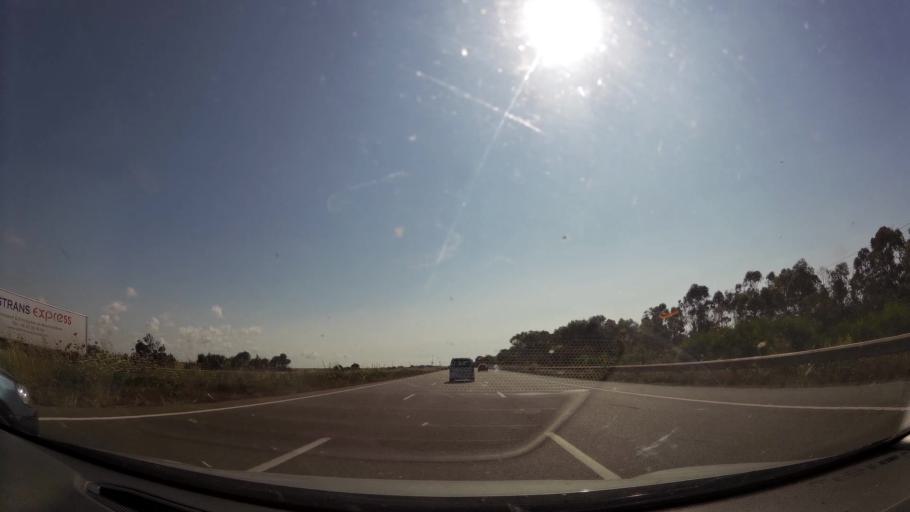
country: MA
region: Chaouia-Ouardigha
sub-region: Benslimane
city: Bouznika
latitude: 33.7890
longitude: -7.2072
